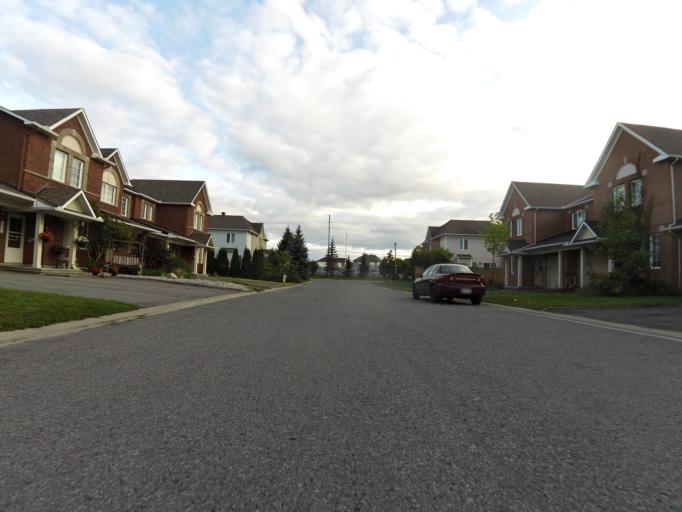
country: CA
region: Ontario
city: Bells Corners
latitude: 45.2767
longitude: -75.7293
